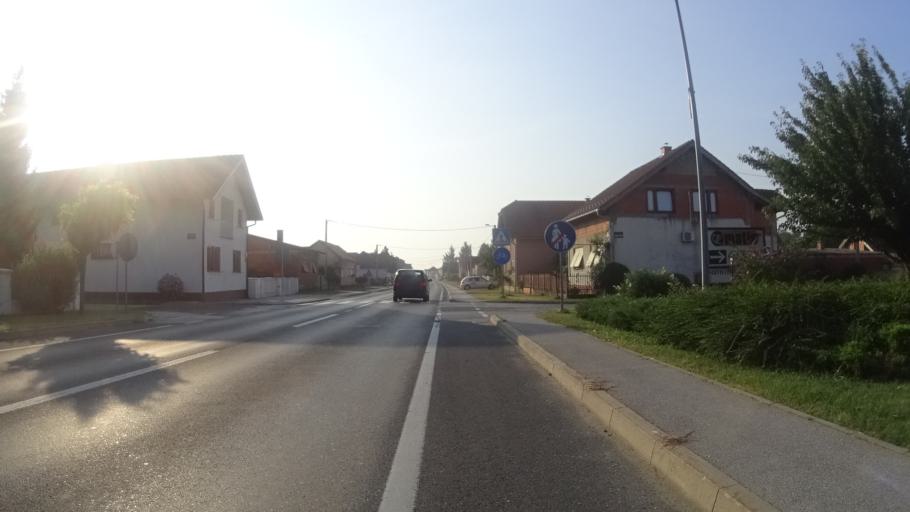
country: HR
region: Varazdinska
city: Sracinec
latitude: 46.3341
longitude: 16.2668
